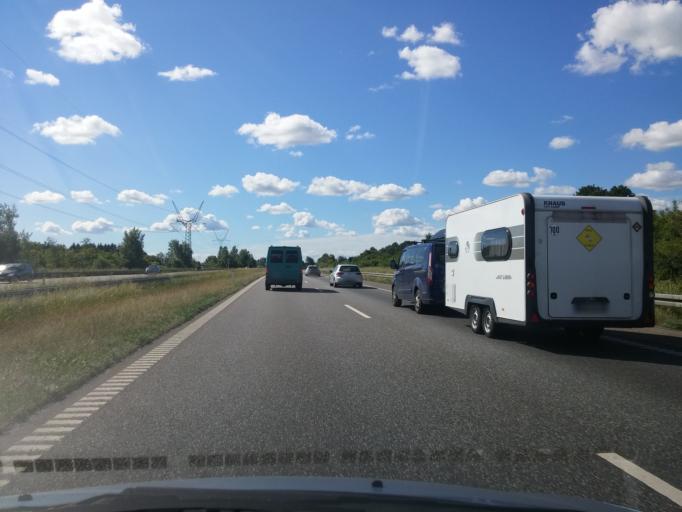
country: DK
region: South Denmark
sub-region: Kolding Kommune
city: Kolding
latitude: 55.4390
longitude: 9.4573
